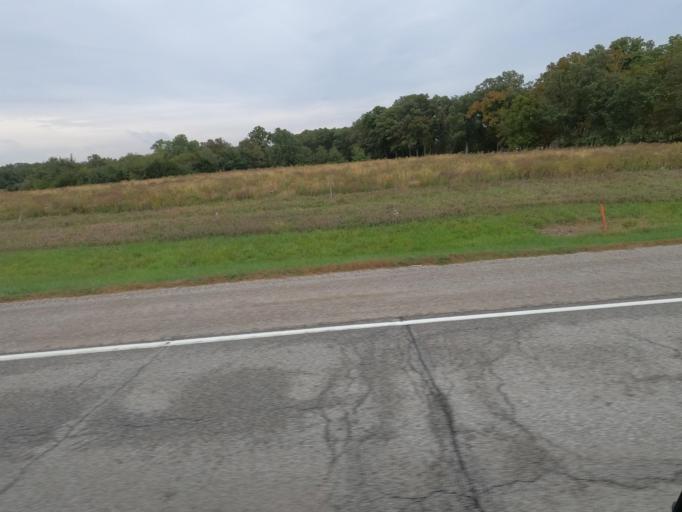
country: US
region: Iowa
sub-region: Van Buren County
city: Keosauqua
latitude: 40.8387
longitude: -92.0071
